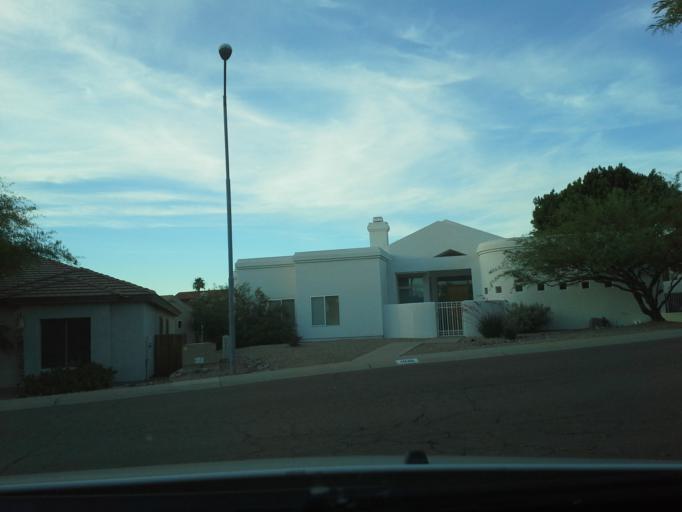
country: US
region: Arizona
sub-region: Maricopa County
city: Paradise Valley
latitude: 33.6257
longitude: -112.0596
